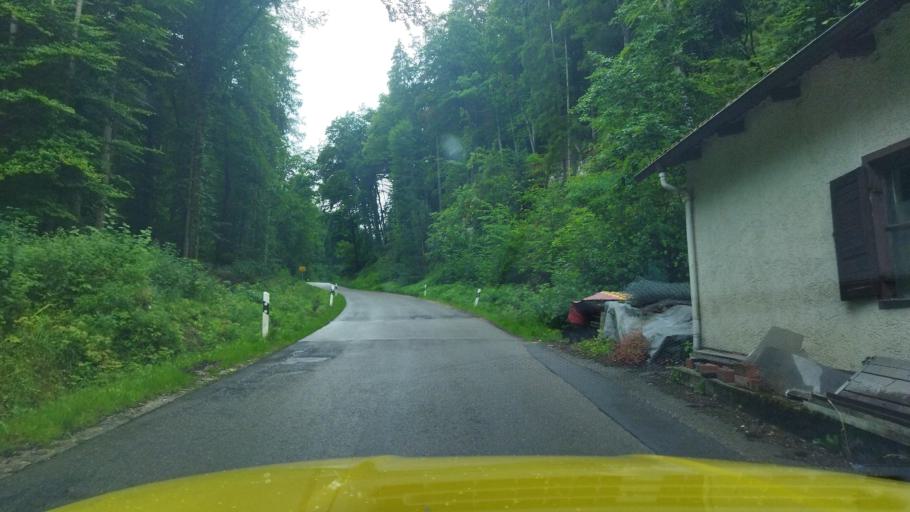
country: DE
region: Bavaria
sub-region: Lower Bavaria
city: Riedenburg
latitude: 48.9457
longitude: 11.7382
